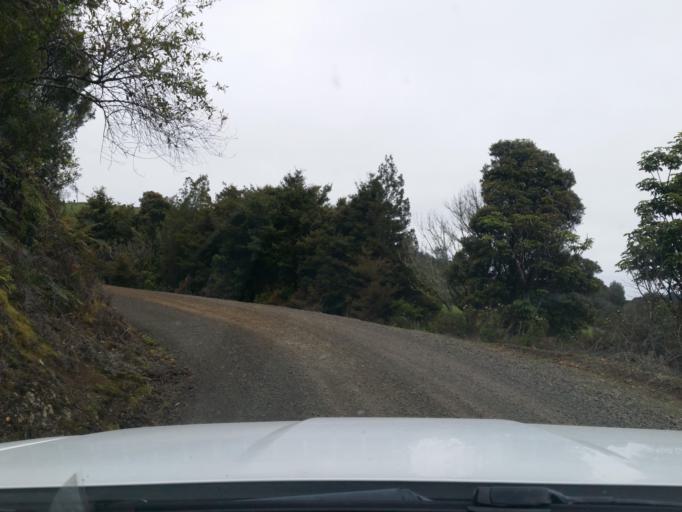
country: NZ
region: Northland
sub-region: Kaipara District
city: Dargaville
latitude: -35.7071
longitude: 173.6379
